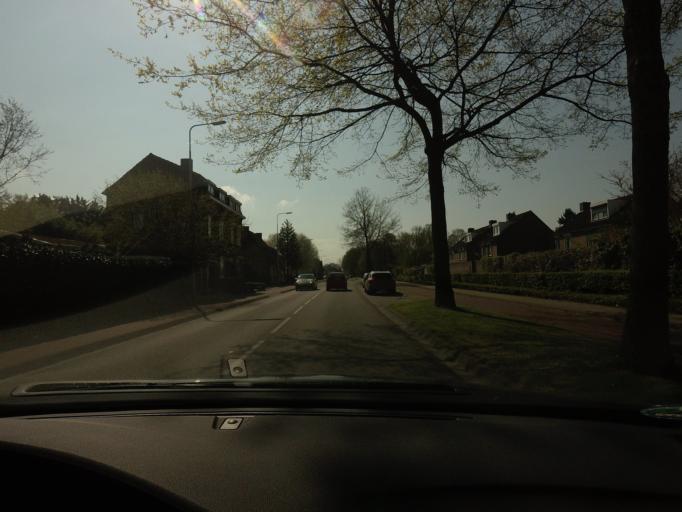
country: NL
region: Limburg
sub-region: Gemeente Maastricht
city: Heer
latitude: 50.8326
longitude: 5.7276
